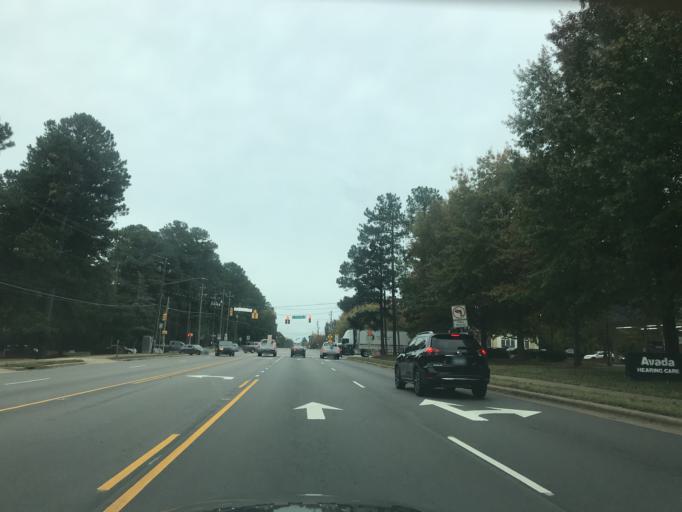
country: US
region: North Carolina
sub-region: Wake County
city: West Raleigh
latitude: 35.8821
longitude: -78.6262
